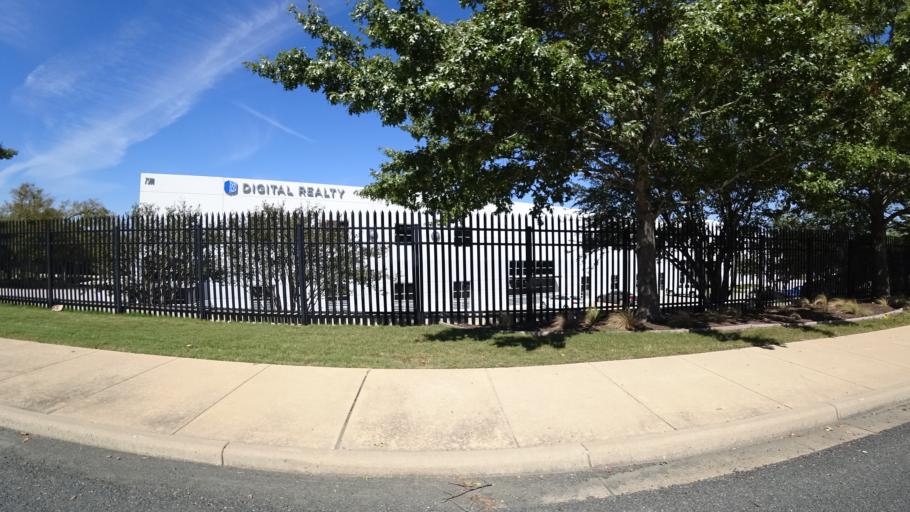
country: US
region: Texas
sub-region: Travis County
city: Austin
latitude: 30.2114
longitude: -97.6958
